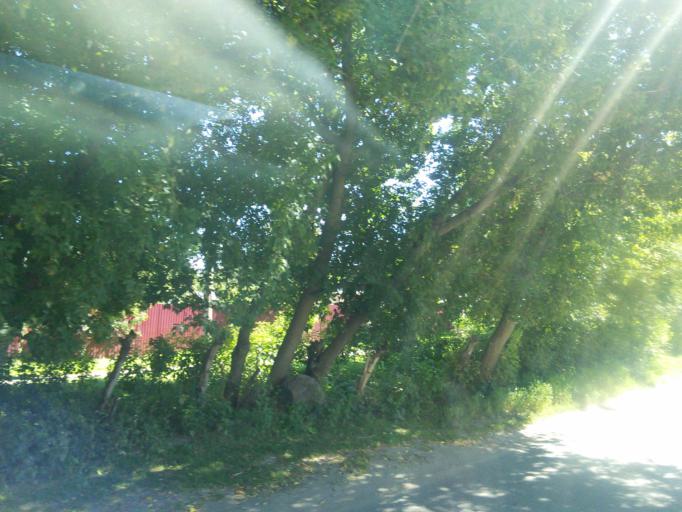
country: RU
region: Tverskaya
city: Kashin
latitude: 57.3609
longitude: 37.6143
